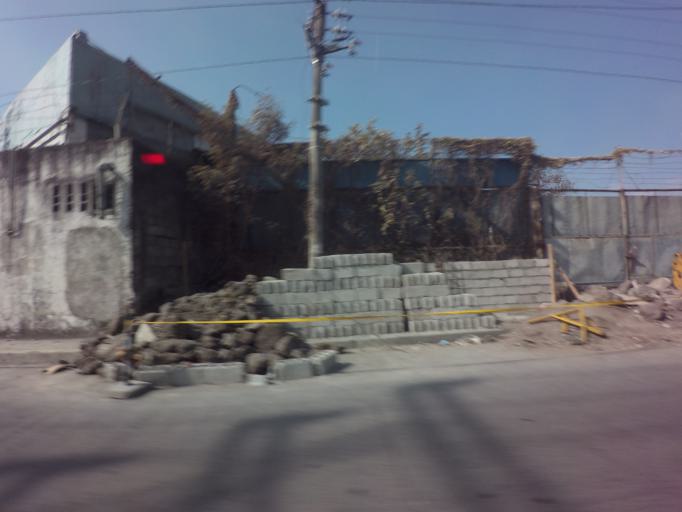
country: PH
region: Calabarzon
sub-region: Province of Rizal
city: Taguig
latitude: 14.5008
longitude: 121.0458
